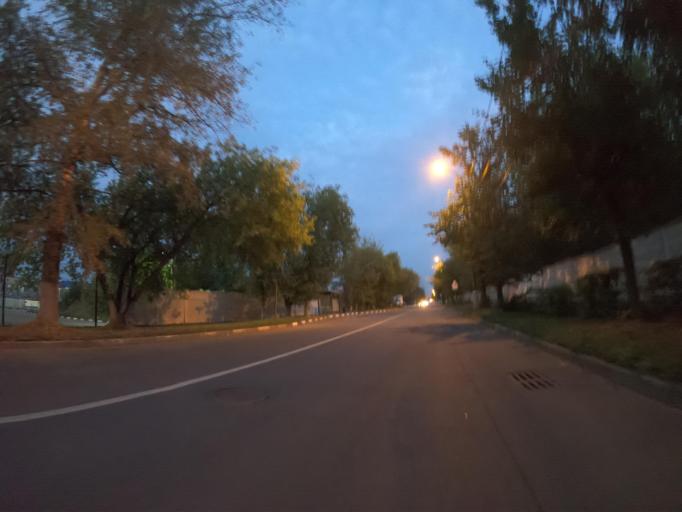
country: RU
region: Moskovskaya
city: Zhukovskiy
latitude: 55.6040
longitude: 38.1188
